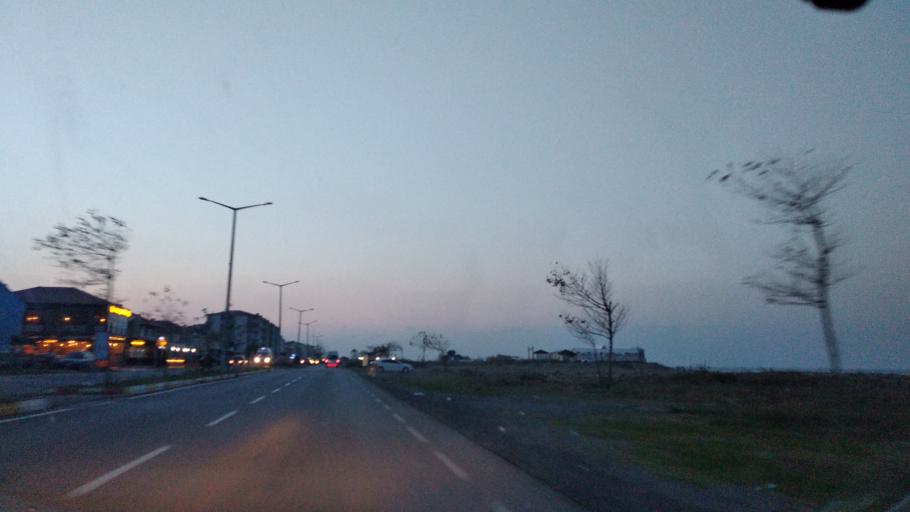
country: TR
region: Sakarya
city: Karasu
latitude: 41.0990
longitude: 30.7231
